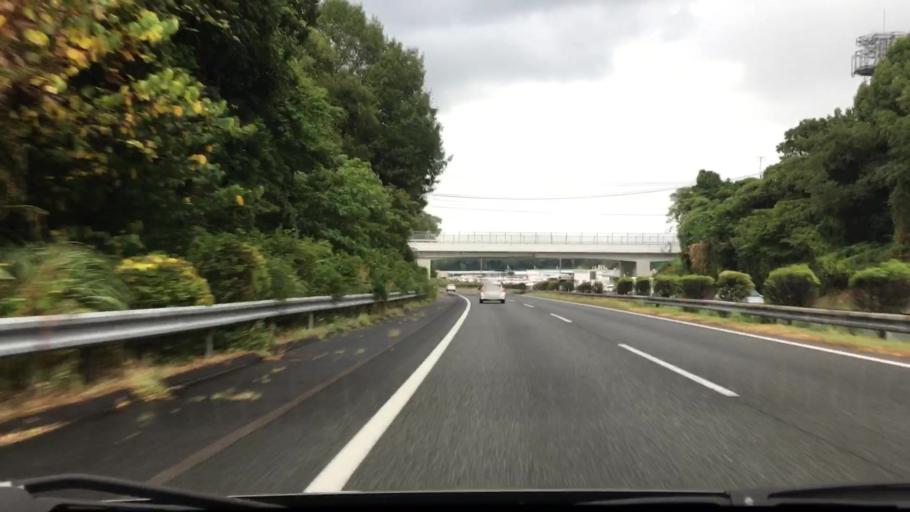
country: JP
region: Fukuoka
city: Miyata
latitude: 33.7455
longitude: 130.6181
